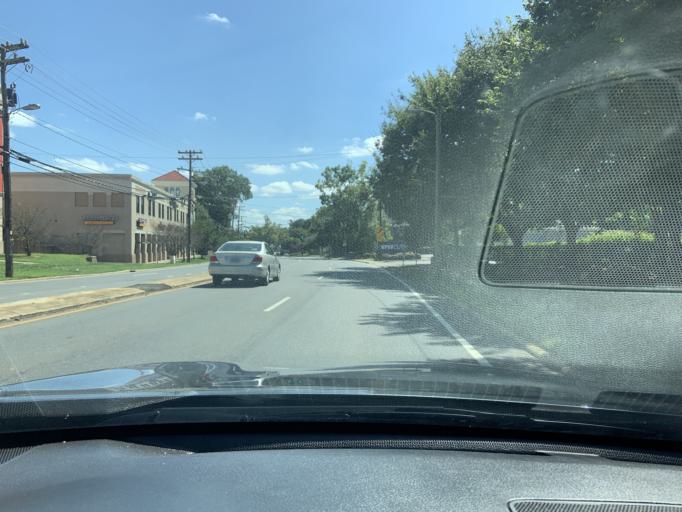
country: US
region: North Carolina
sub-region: Mecklenburg County
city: Charlotte
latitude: 35.1664
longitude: -80.8505
